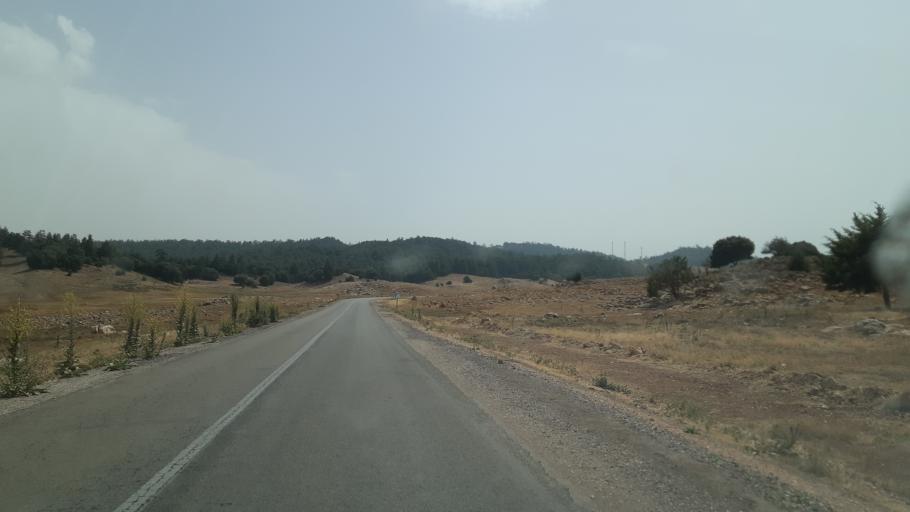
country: MA
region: Meknes-Tafilalet
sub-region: Ifrane
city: Ifrane
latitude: 33.4295
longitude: -5.0648
